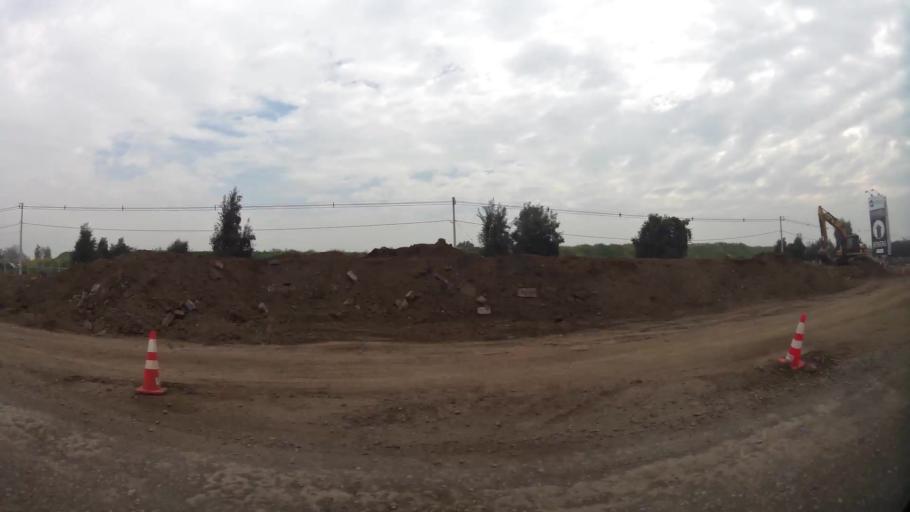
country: CL
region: Santiago Metropolitan
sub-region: Provincia de Chacabuco
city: Chicureo Abajo
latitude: -33.2233
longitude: -70.6797
